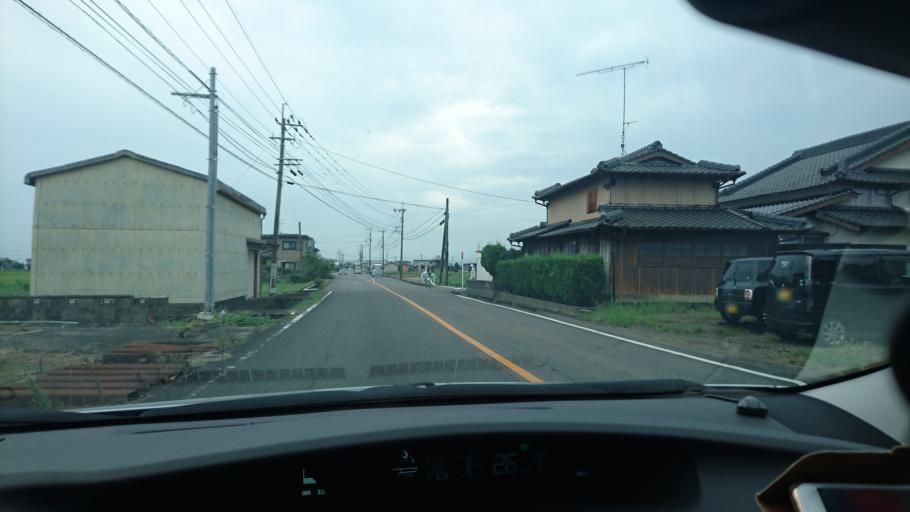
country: JP
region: Saga Prefecture
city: Takeocho-takeo
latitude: 33.2120
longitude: 130.1207
